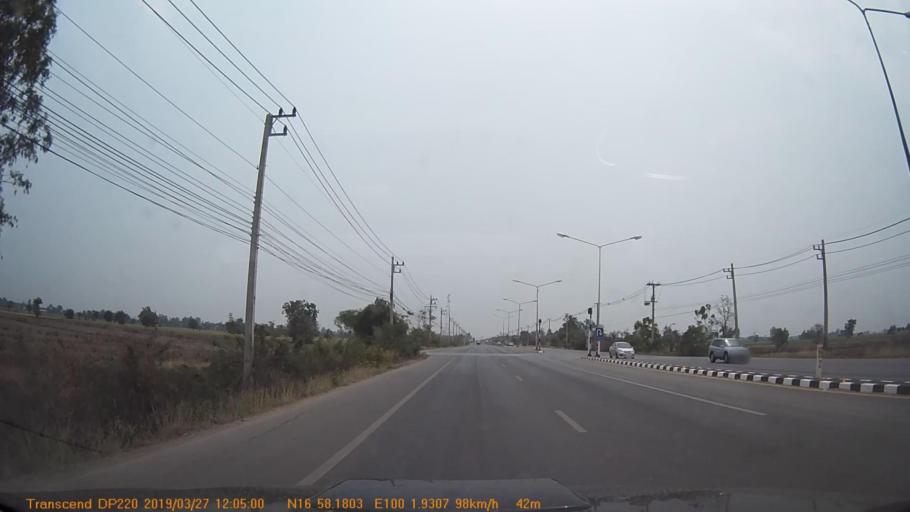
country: TH
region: Sukhothai
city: Kong Krailat
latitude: 16.9696
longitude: 100.0326
